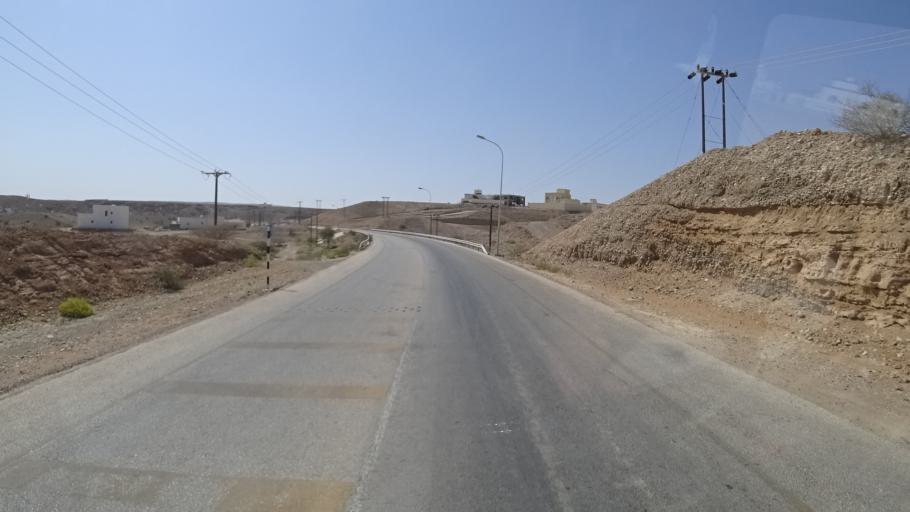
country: OM
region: Ash Sharqiyah
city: Sur
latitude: 22.5446
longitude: 59.5011
